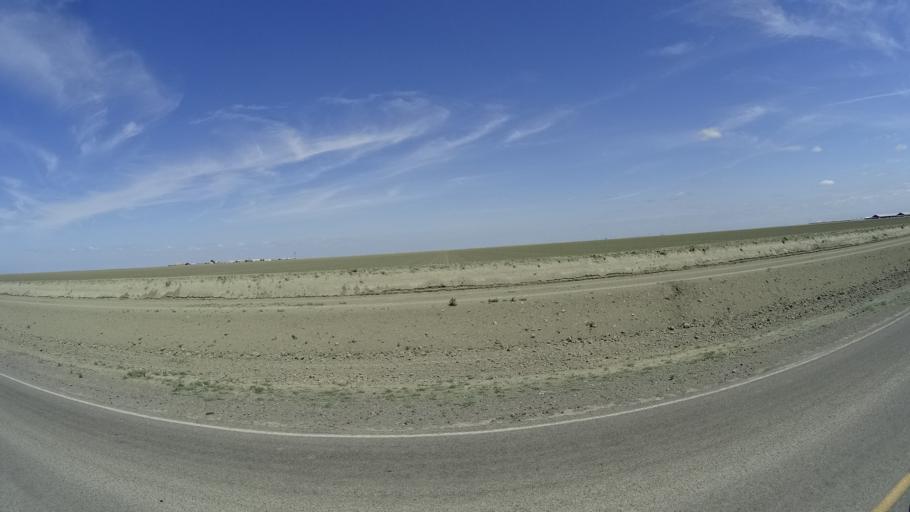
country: US
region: California
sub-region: Tulare County
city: Alpaugh
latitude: 35.9342
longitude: -119.5835
